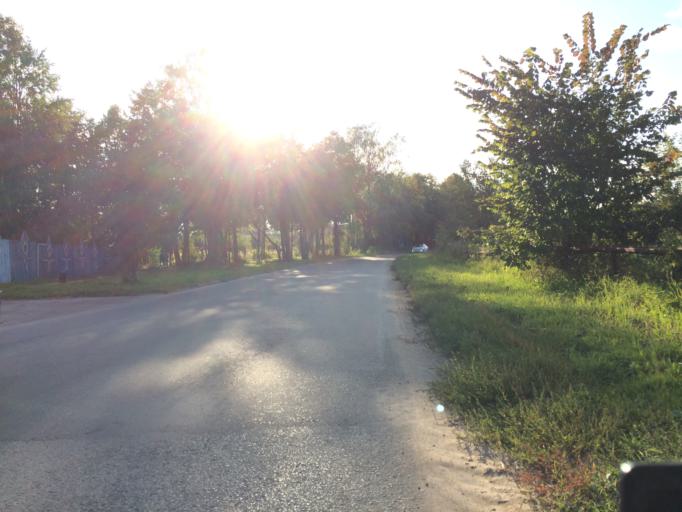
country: RU
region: Mariy-El
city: Yoshkar-Ola
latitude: 56.6493
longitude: 47.9642
